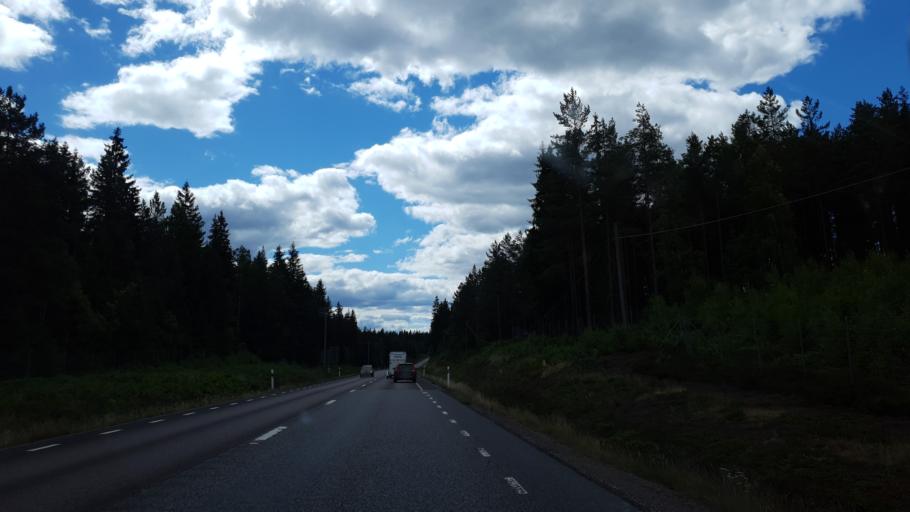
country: SE
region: Kronoberg
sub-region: Vaxjo Kommun
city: Braas
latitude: 57.1781
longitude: 15.1591
